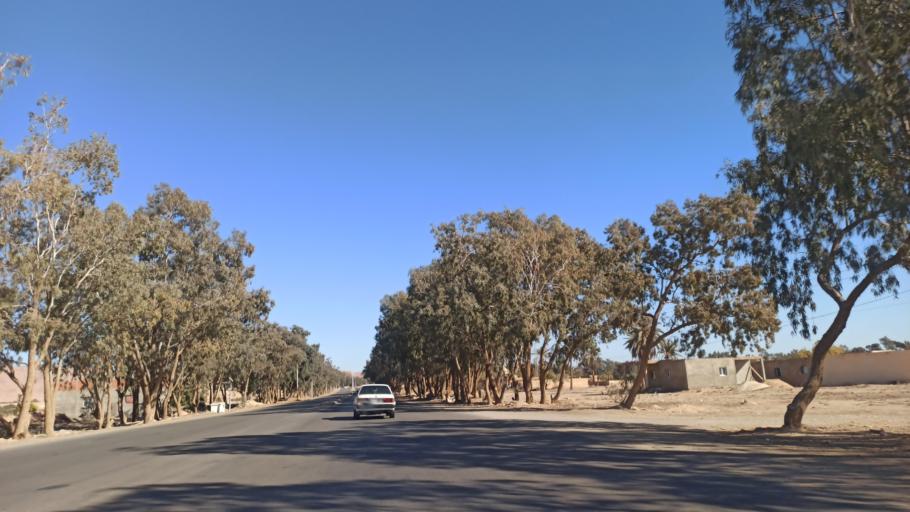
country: TN
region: Gafsa
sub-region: Gafsa Municipality
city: Gafsa
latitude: 34.3973
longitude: 8.7195
